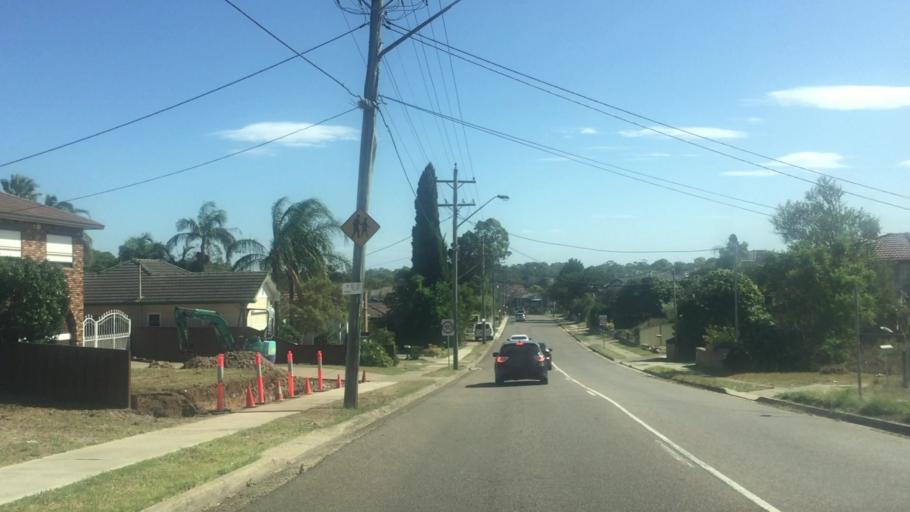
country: AU
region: New South Wales
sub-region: Holroyd
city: Merrylands
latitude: -33.8279
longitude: 150.9807
